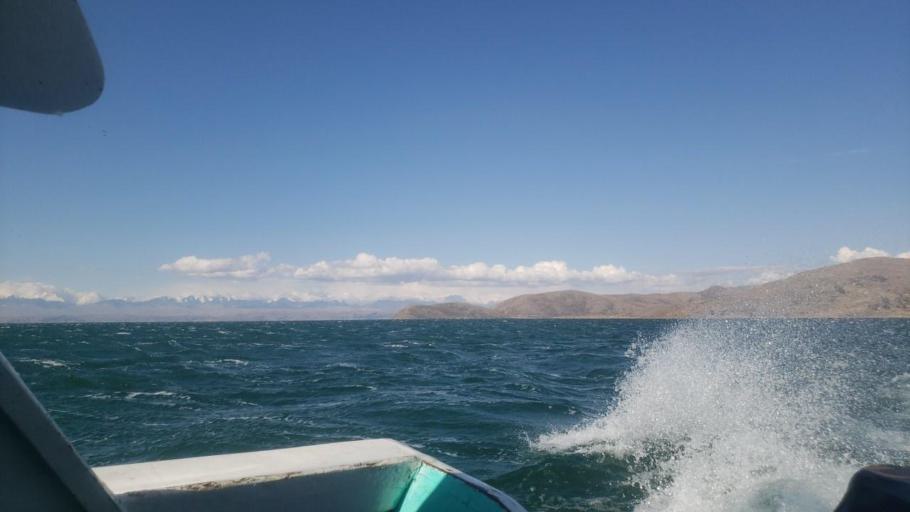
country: BO
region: La Paz
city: Huatajata
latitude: -16.3199
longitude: -68.7361
